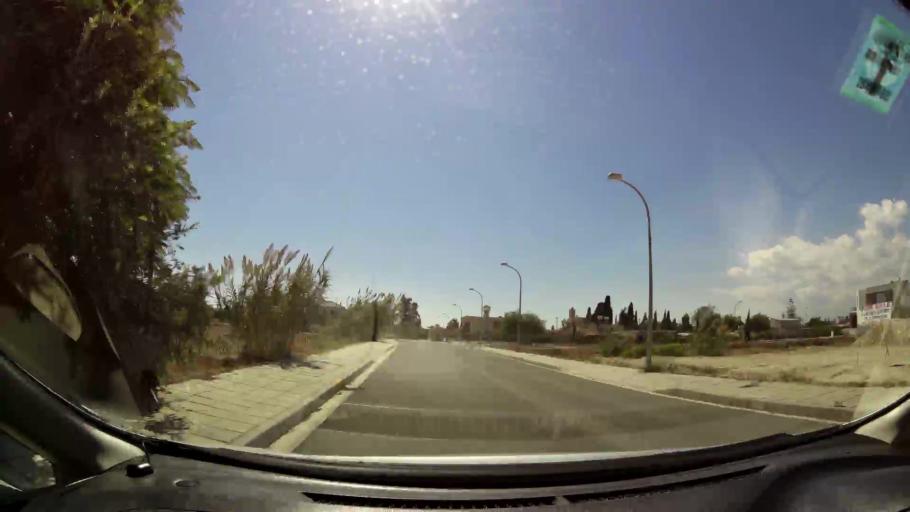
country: CY
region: Larnaka
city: Livadia
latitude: 34.9572
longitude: 33.6284
